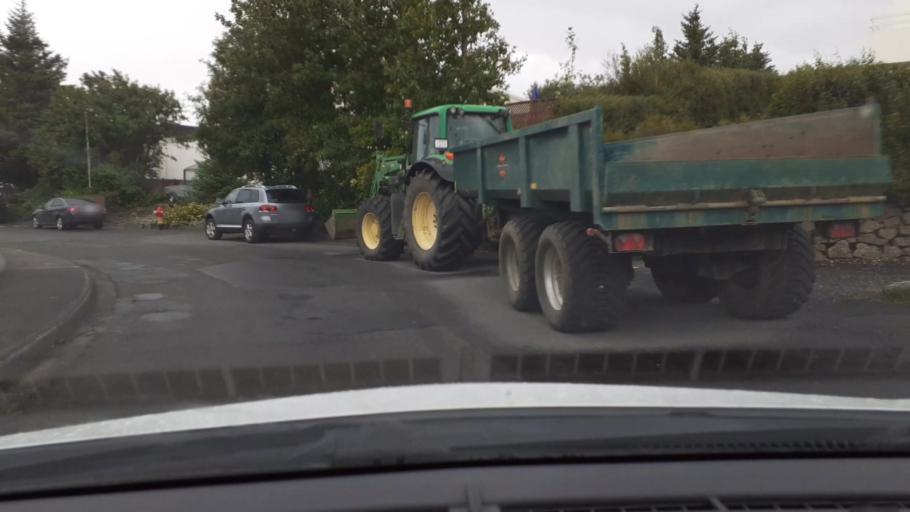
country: IS
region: West
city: Borgarnes
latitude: 64.5404
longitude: -21.9144
